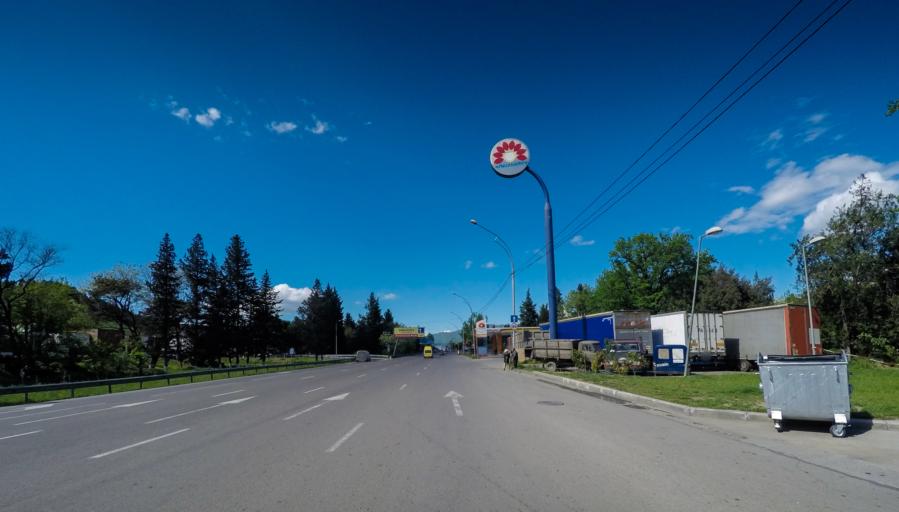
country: GE
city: Zahesi
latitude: 41.7678
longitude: 44.7693
